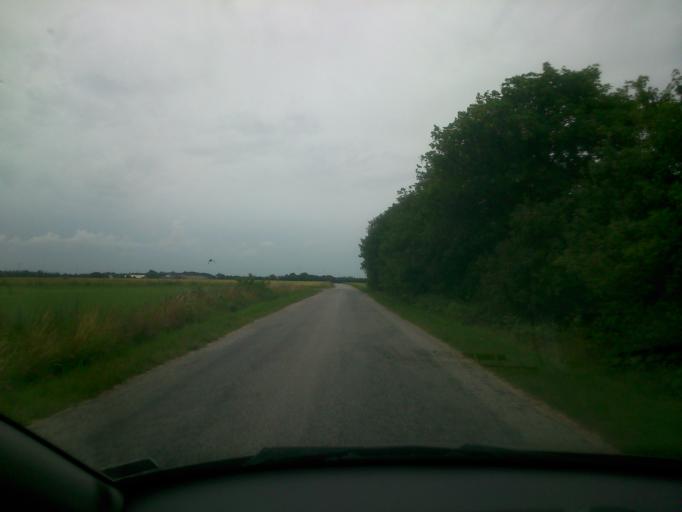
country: DK
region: South Denmark
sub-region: Esbjerg Kommune
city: Esbjerg
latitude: 55.5413
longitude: 8.4304
